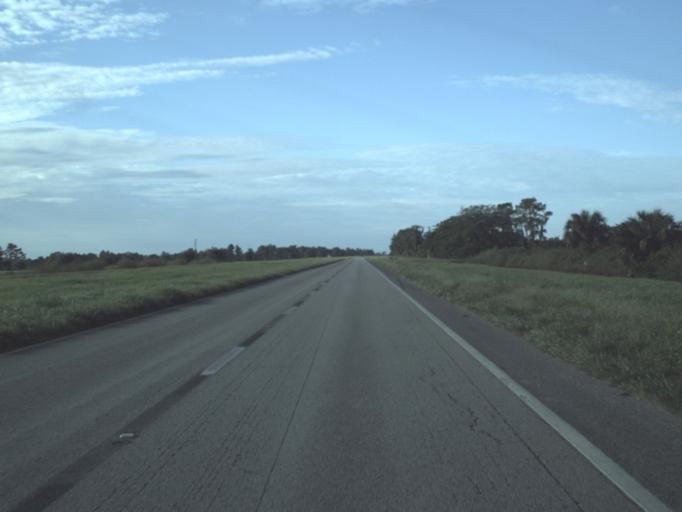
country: US
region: Florida
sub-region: Highlands County
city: Placid Lakes
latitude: 27.0844
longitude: -81.3347
